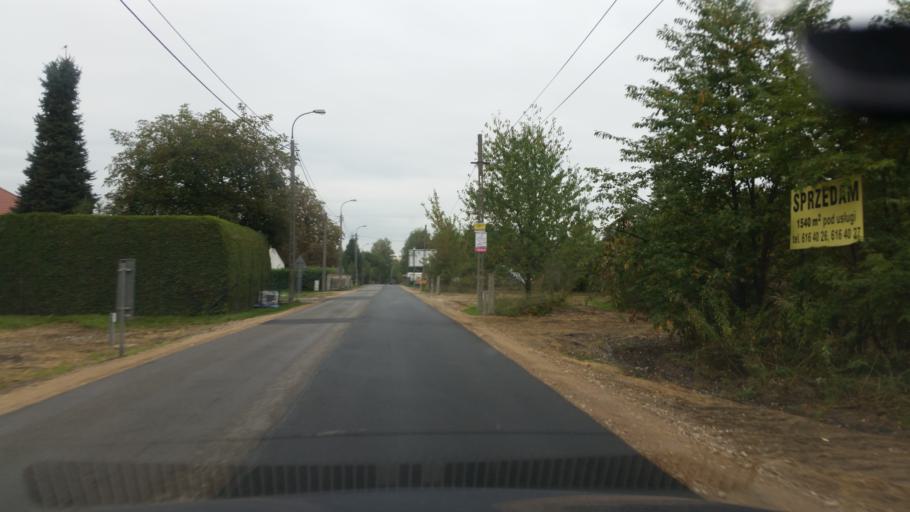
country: PL
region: Masovian Voivodeship
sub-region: Powiat piaseczynski
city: Jozefoslaw
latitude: 52.0957
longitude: 21.0784
